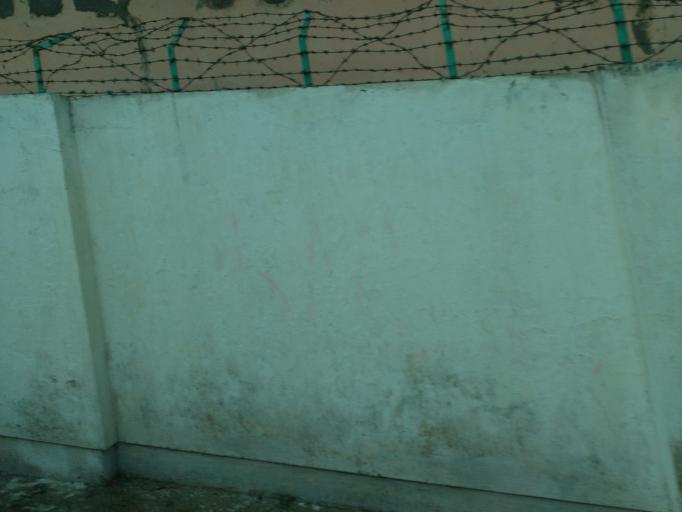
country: ID
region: Central Java
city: Delanggu
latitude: -7.6166
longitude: 110.6999
